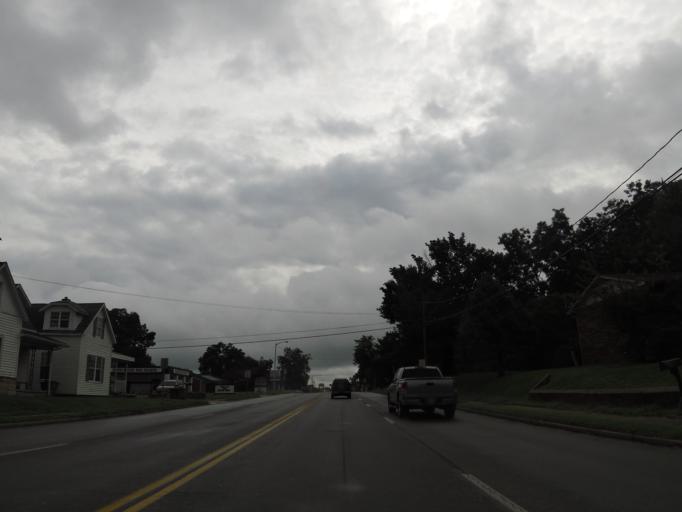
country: US
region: Missouri
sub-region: Cape Girardeau County
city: Cape Girardeau
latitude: 37.3015
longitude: -89.5318
